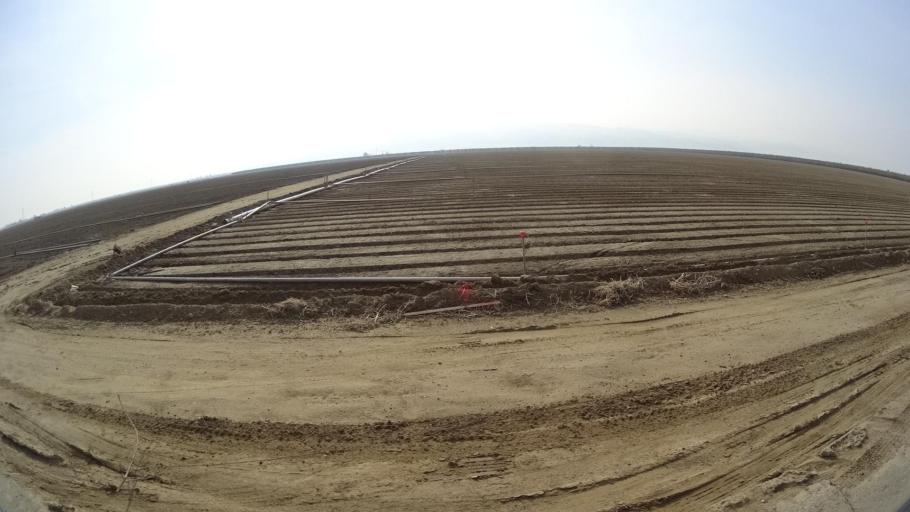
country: US
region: California
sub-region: Kern County
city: Weedpatch
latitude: 35.0763
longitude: -118.9984
